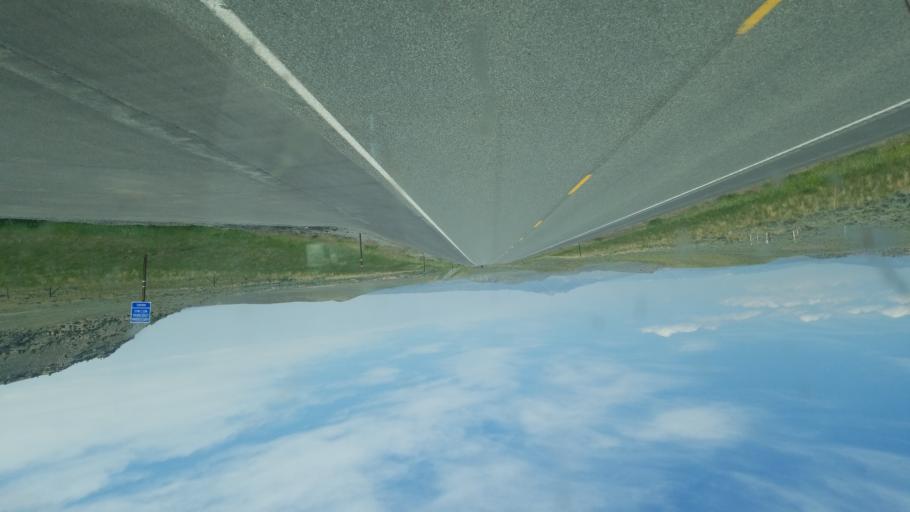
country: US
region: Wyoming
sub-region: Park County
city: Cody
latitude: 44.4139
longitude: -109.0078
